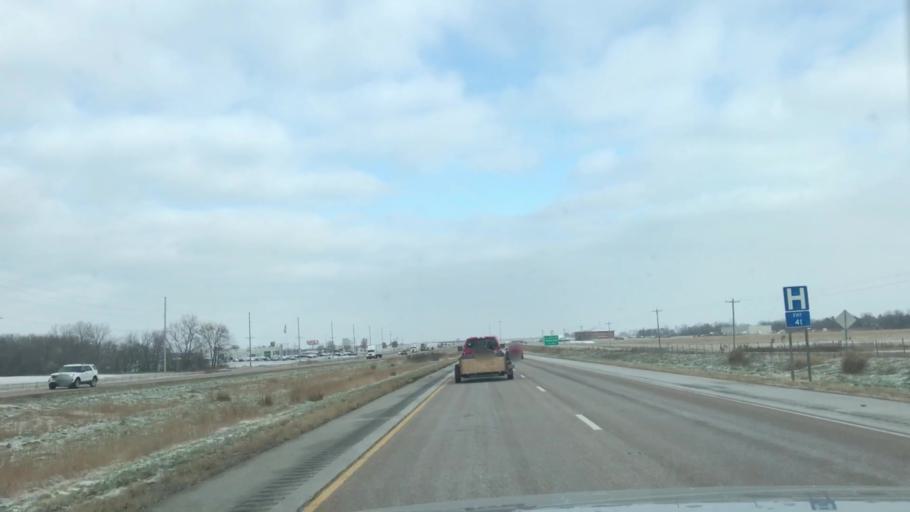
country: US
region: Illinois
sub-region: Macoupin County
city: Staunton
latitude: 39.0080
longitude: -89.7496
